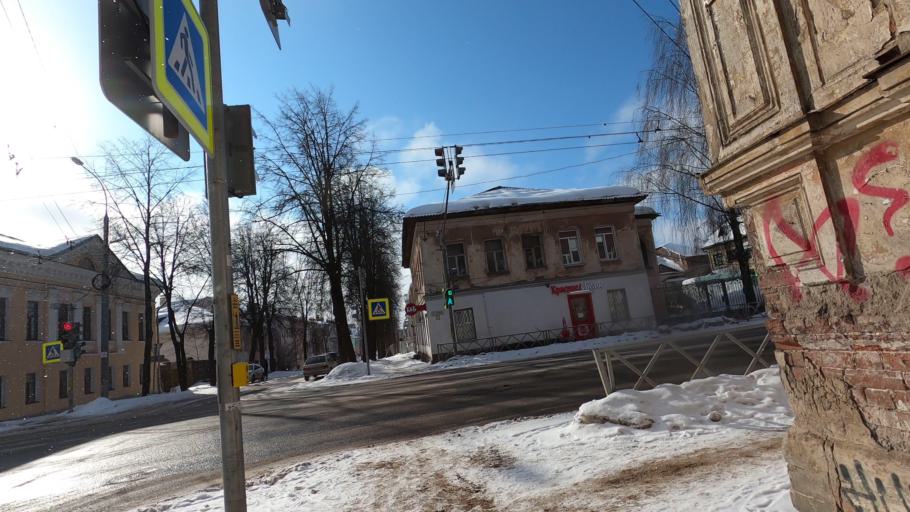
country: RU
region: Jaroslavl
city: Rybinsk
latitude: 58.0469
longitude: 38.8483
